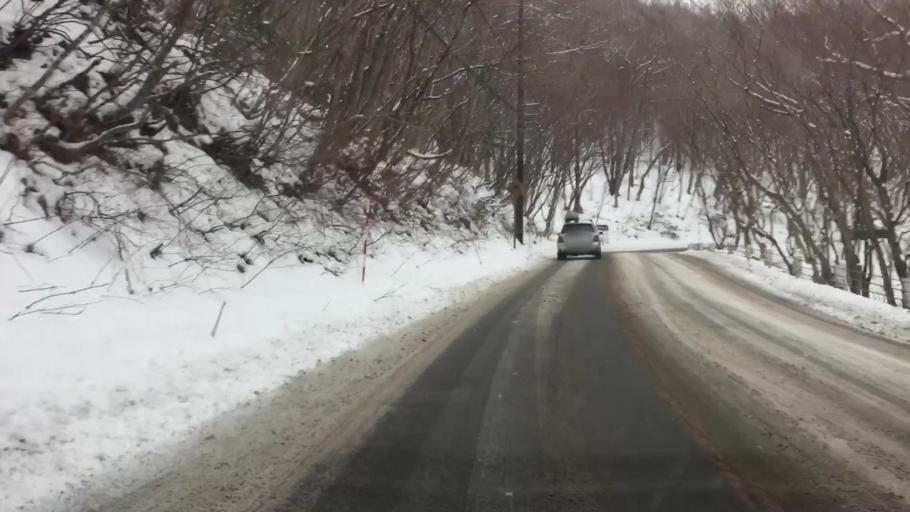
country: JP
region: Tochigi
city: Yaita
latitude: 36.9693
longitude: 139.7927
